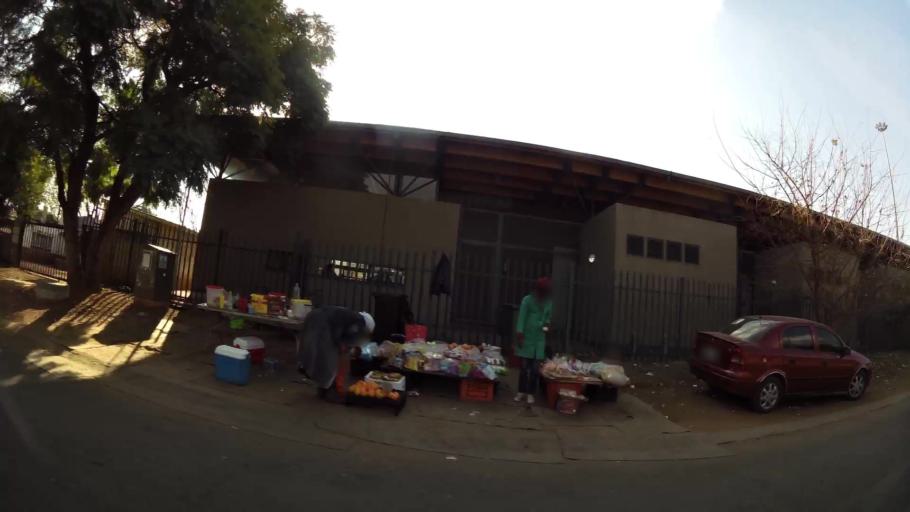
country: ZA
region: Gauteng
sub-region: Ekurhuleni Metropolitan Municipality
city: Tembisa
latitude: -25.9564
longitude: 28.2283
